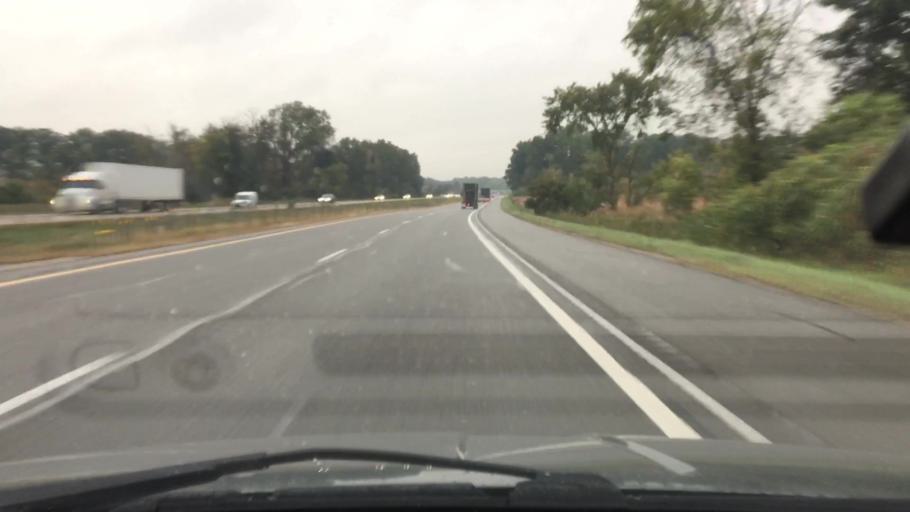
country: US
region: Michigan
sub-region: Jackson County
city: Grass Lake
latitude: 42.2966
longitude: -84.1330
